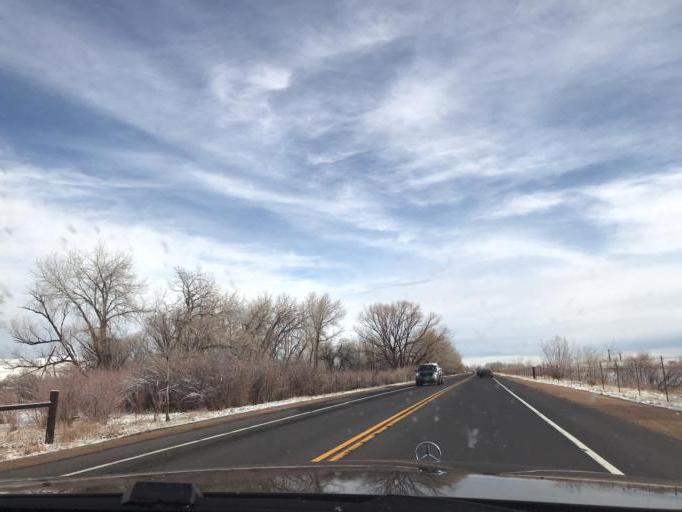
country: US
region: Colorado
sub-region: Boulder County
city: Superior
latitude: 39.9903
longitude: -105.2127
